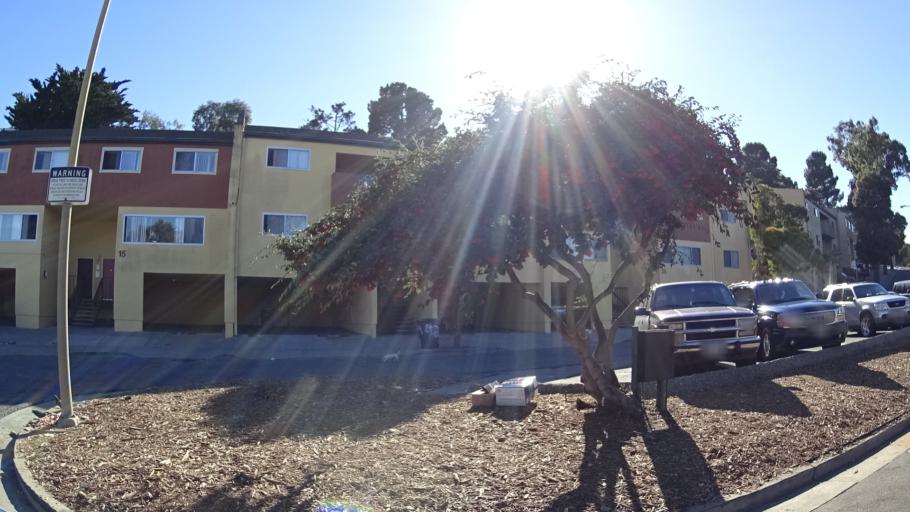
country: US
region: California
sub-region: San Francisco County
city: San Francisco
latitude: 37.7357
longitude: -122.3821
